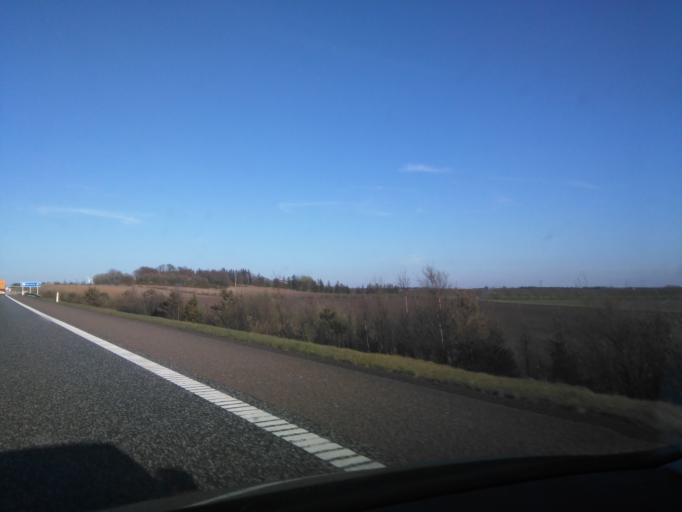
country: DK
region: Central Jutland
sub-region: Ikast-Brande Kommune
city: Bording Kirkeby
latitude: 56.1341
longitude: 9.2532
